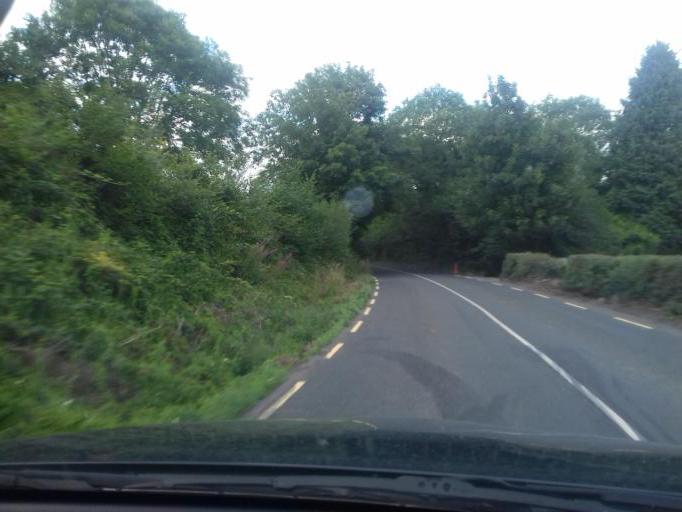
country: IE
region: Leinster
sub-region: Kilkenny
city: Graiguenamanagh
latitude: 52.5053
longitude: -6.9473
